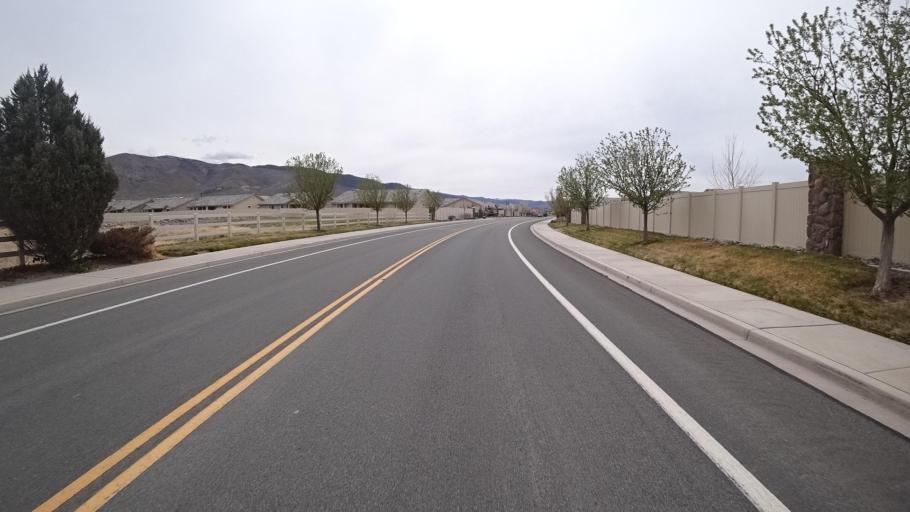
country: US
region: Nevada
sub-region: Washoe County
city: Sparks
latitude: 39.4369
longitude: -119.7208
